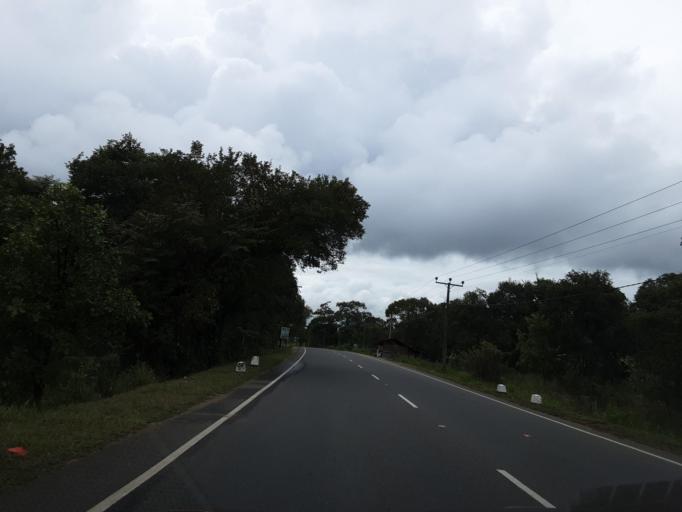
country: LK
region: Uva
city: Badulla
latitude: 7.3991
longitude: 81.1037
